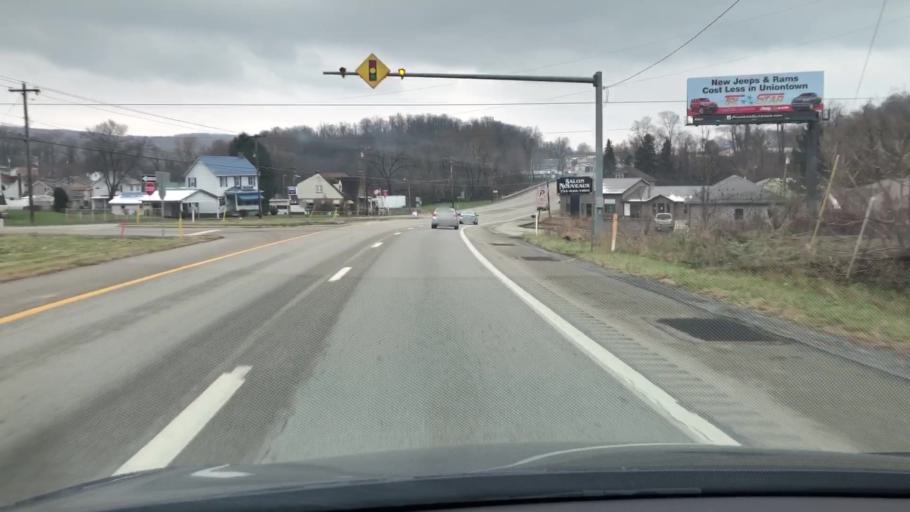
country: US
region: Pennsylvania
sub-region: Fayette County
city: Connellsville
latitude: 40.0049
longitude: -79.6028
